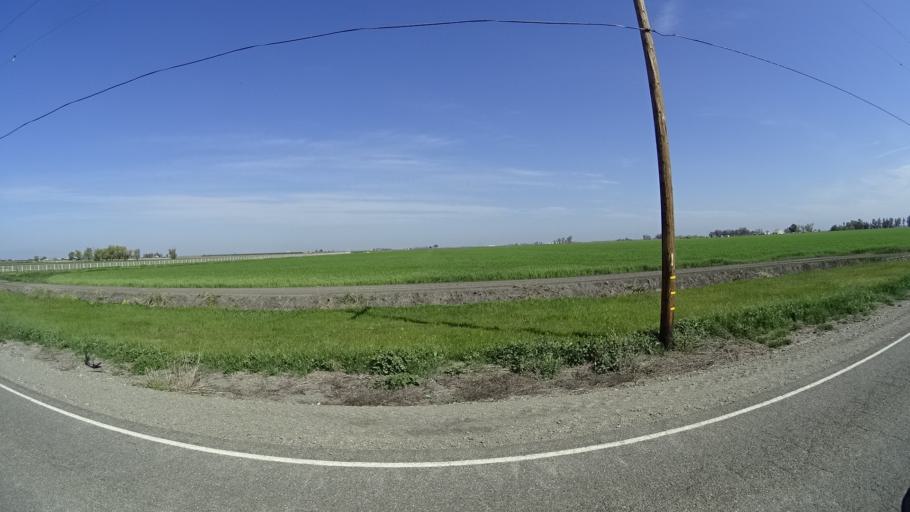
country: US
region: California
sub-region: Glenn County
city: Willows
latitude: 39.5828
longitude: -122.0736
